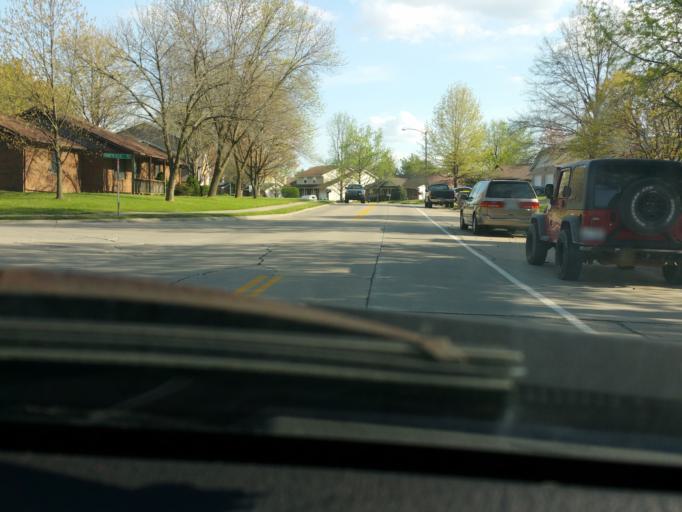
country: US
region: Illinois
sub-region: Madison County
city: Edwardsville
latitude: 38.7924
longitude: -89.9681
